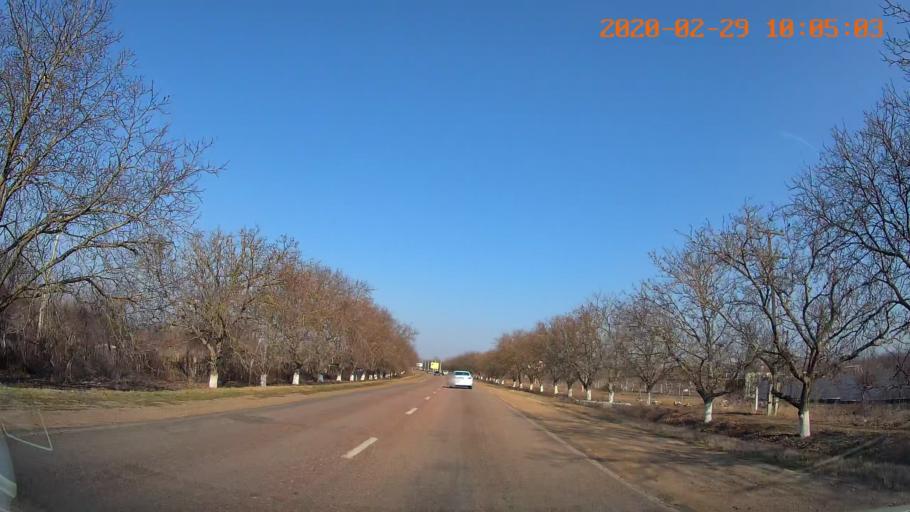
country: MD
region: Telenesti
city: Tiraspolul Nou
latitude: 46.8037
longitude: 29.6733
